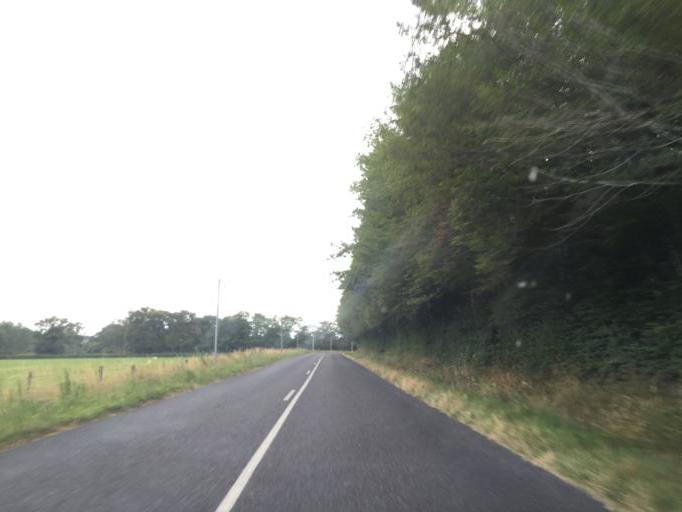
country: FR
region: Auvergne
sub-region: Departement de l'Allier
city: Lusigny
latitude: 46.5286
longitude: 3.4713
